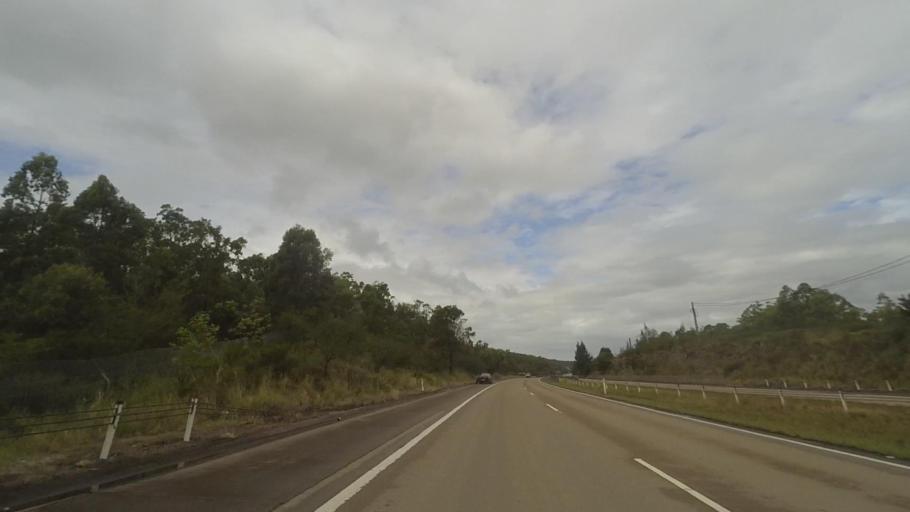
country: AU
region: New South Wales
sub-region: Port Stephens Shire
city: Medowie
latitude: -32.6237
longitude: 151.9486
